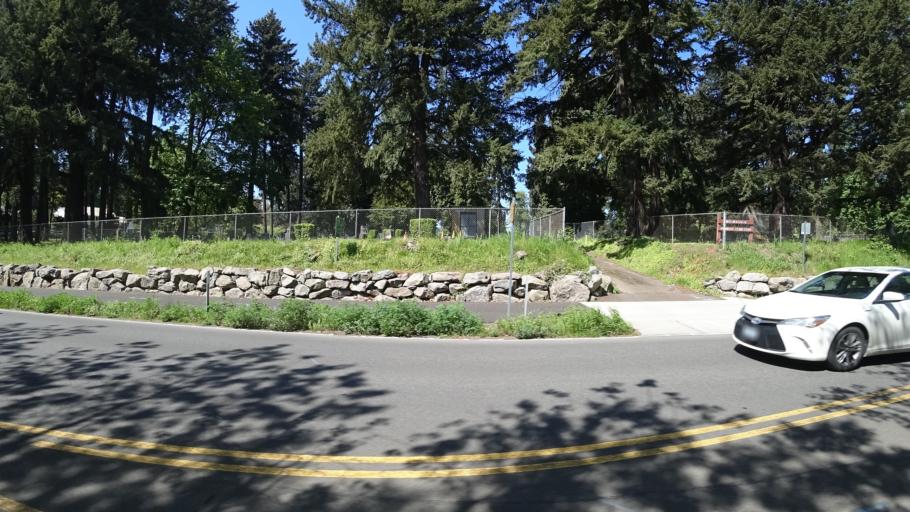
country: US
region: Oregon
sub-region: Clackamas County
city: Milwaukie
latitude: 45.4537
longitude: -122.6462
